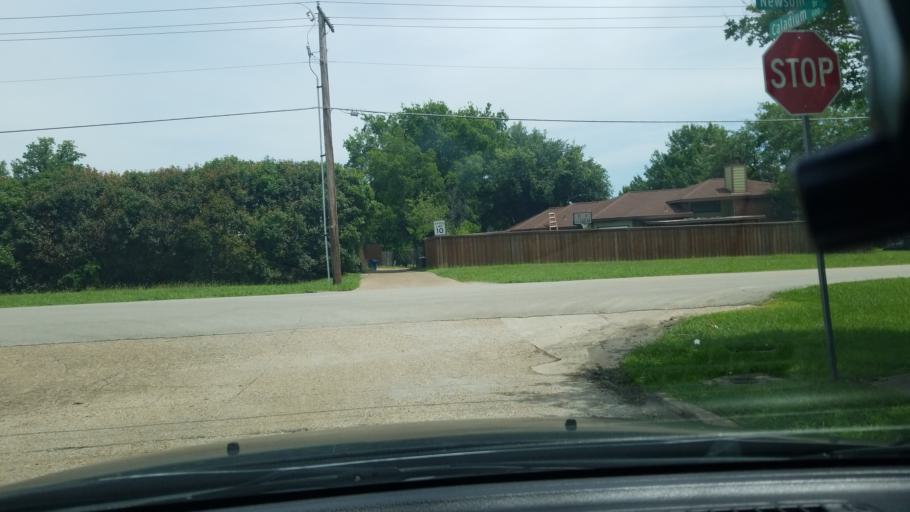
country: US
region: Texas
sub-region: Dallas County
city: Mesquite
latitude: 32.7603
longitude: -96.5801
